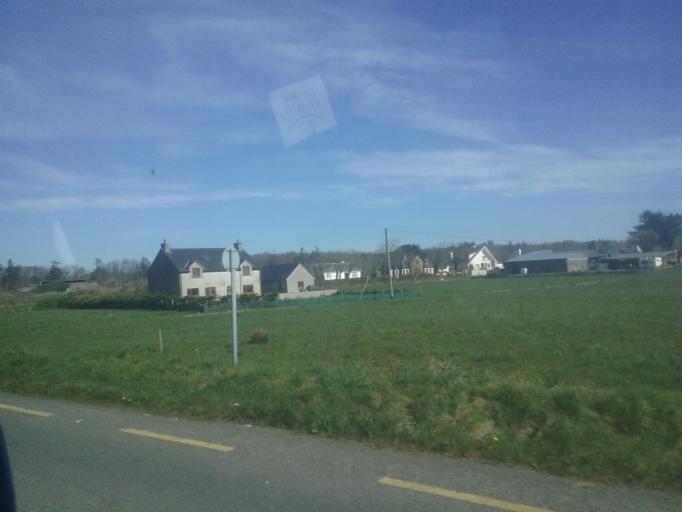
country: IE
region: Munster
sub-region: An Clar
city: Kilrush
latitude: 52.6234
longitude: -9.4662
